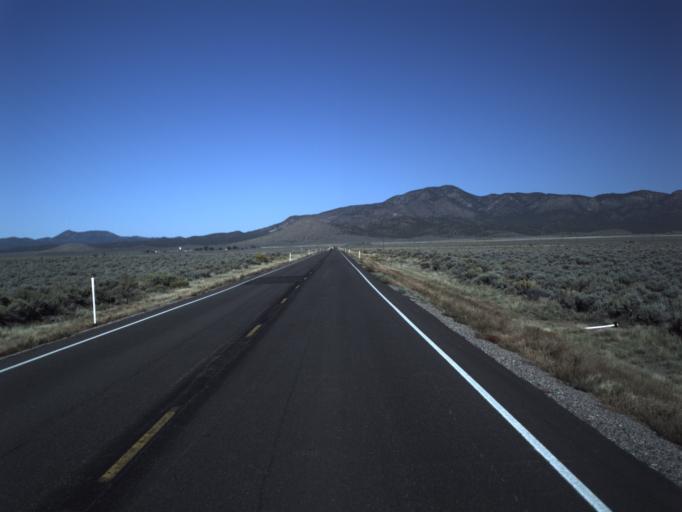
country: US
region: Utah
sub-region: Washington County
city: Enterprise
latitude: 37.7909
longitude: -113.8887
